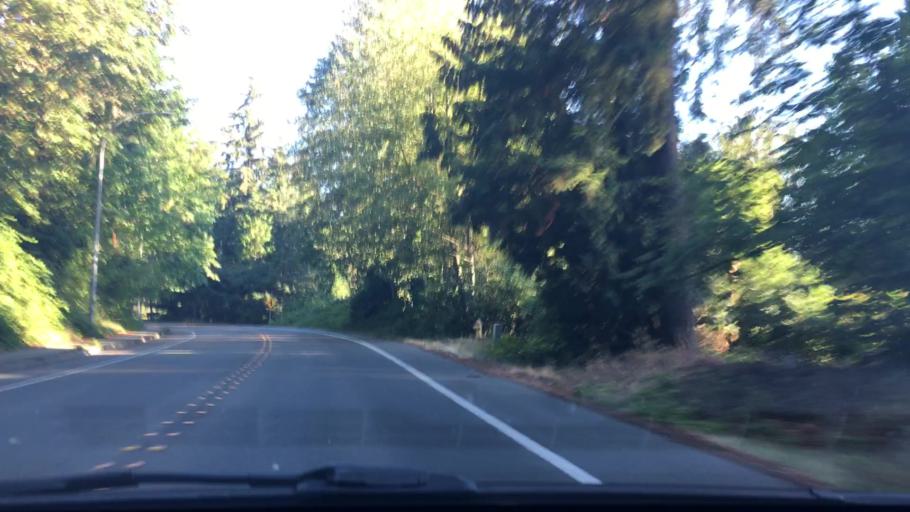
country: US
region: Washington
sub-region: King County
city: Sammamish
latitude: 47.6203
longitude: -122.1108
